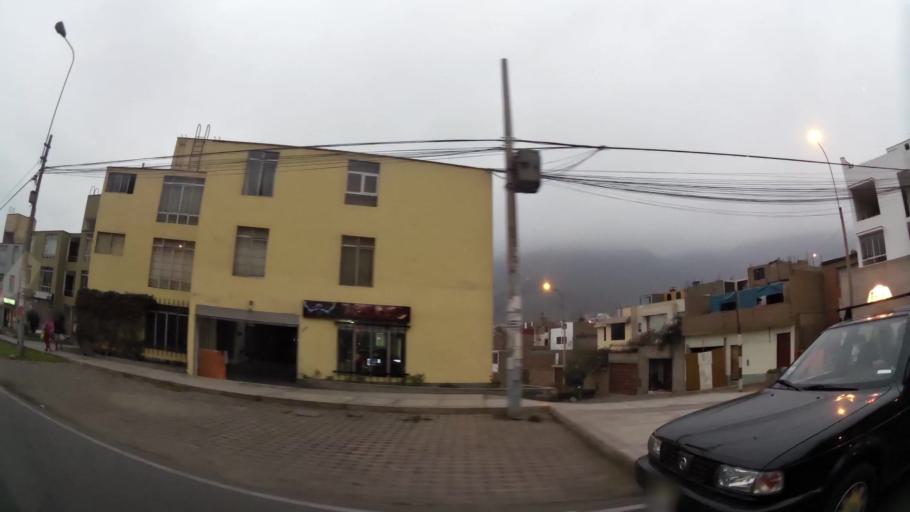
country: PE
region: Lima
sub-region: Lima
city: La Molina
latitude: -12.1130
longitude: -76.9417
